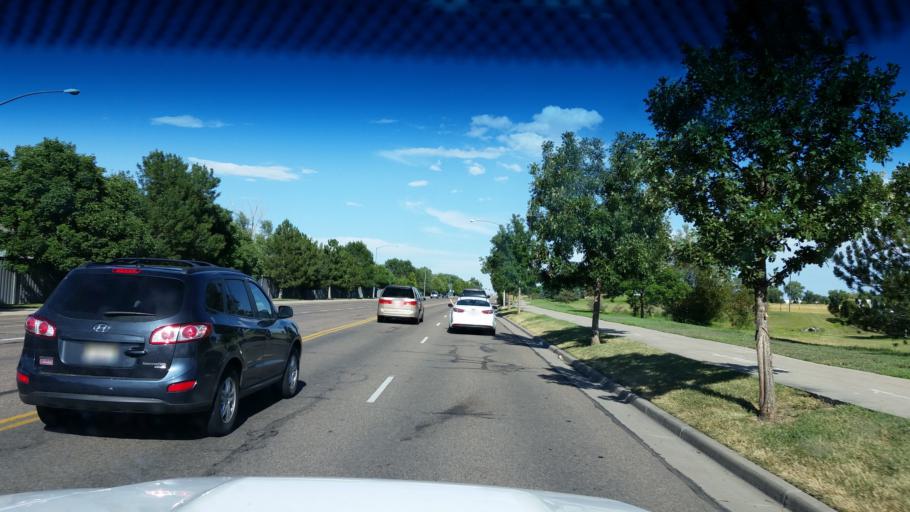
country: US
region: Colorado
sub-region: Adams County
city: Northglenn
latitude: 39.9284
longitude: -104.9769
